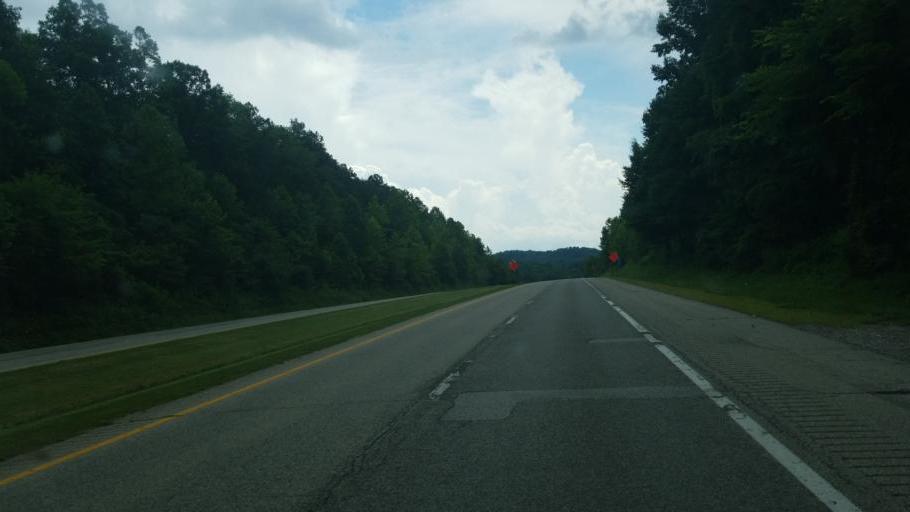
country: US
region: West Virginia
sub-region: Kanawha County
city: Alum Creek
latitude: 38.2716
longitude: -81.7848
